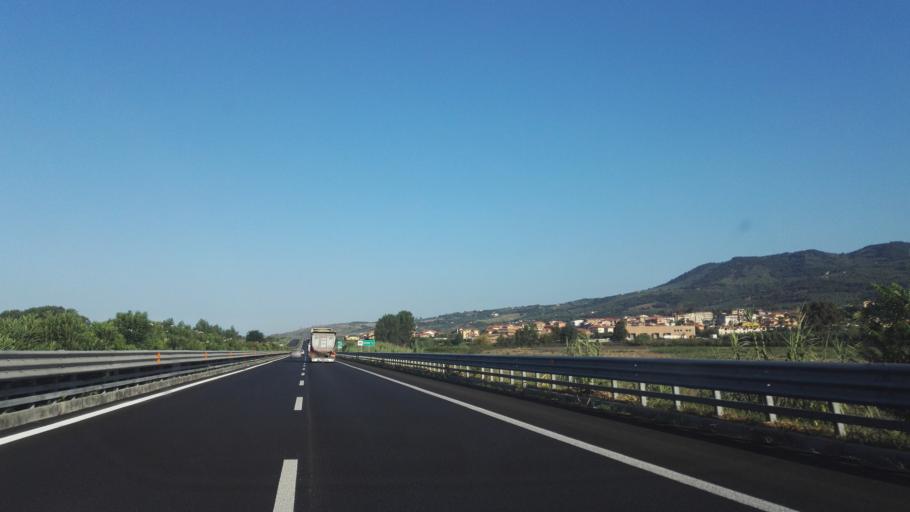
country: IT
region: Calabria
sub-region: Provincia di Catanzaro
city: Santa Eufemia Lamezia
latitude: 38.9350
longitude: 16.2178
